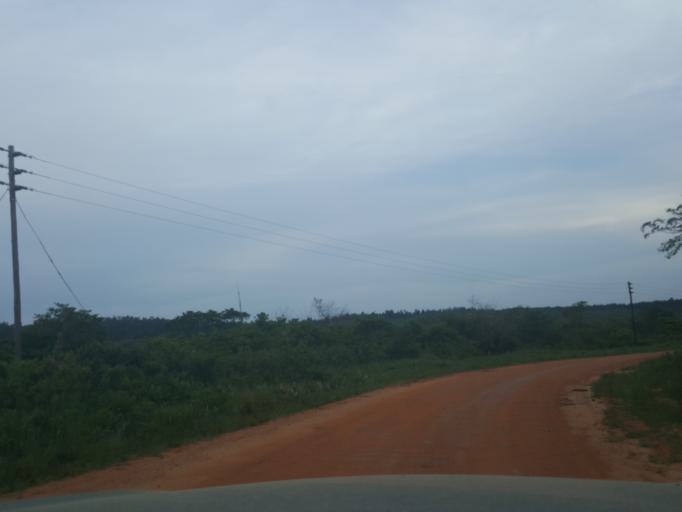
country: ZA
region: Limpopo
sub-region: Mopani District Municipality
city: Hoedspruit
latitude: -24.5965
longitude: 30.9262
